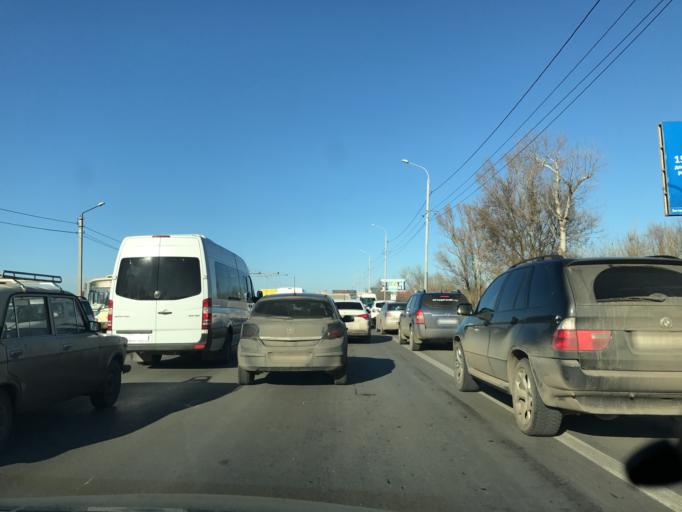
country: RU
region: Rostov
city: Rostov-na-Donu
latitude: 47.1974
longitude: 39.7308
